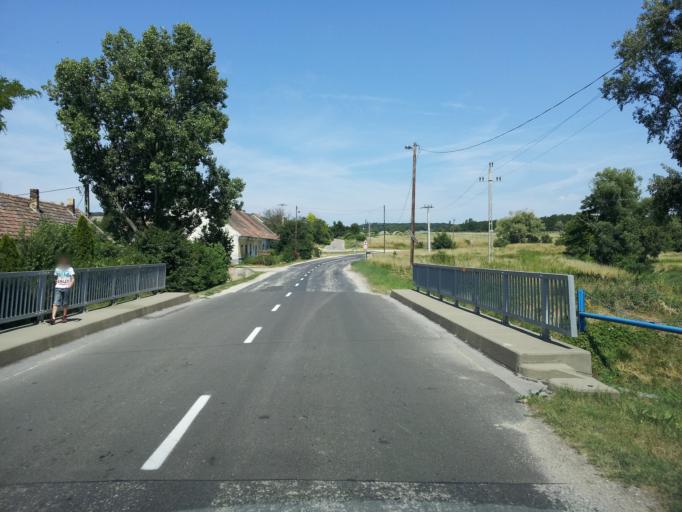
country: HU
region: Fejer
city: Szarliget
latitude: 47.4937
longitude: 18.5659
